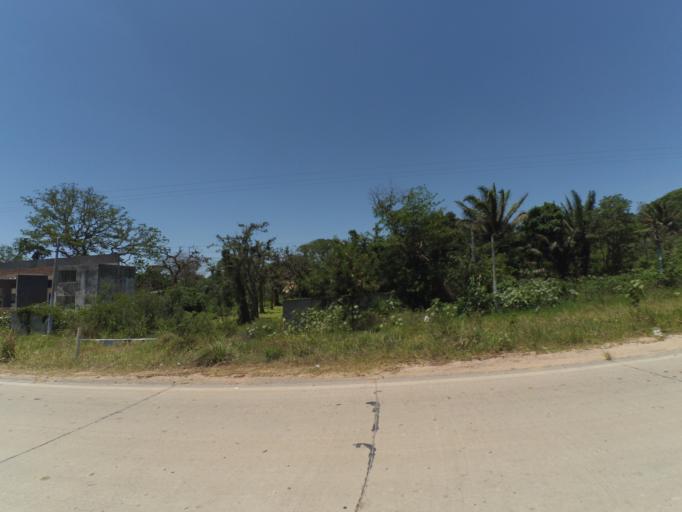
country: BO
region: Santa Cruz
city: Santa Cruz de la Sierra
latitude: -17.7613
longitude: -63.2276
